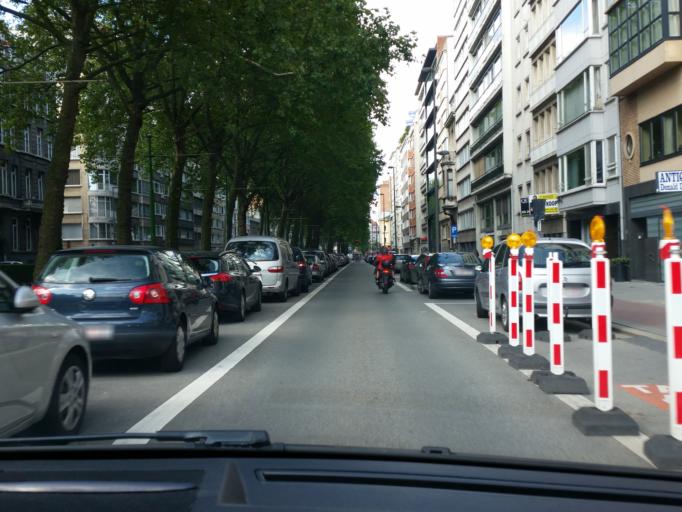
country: BE
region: Flanders
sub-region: Provincie Antwerpen
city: Antwerpen
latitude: 51.2023
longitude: 4.4124
